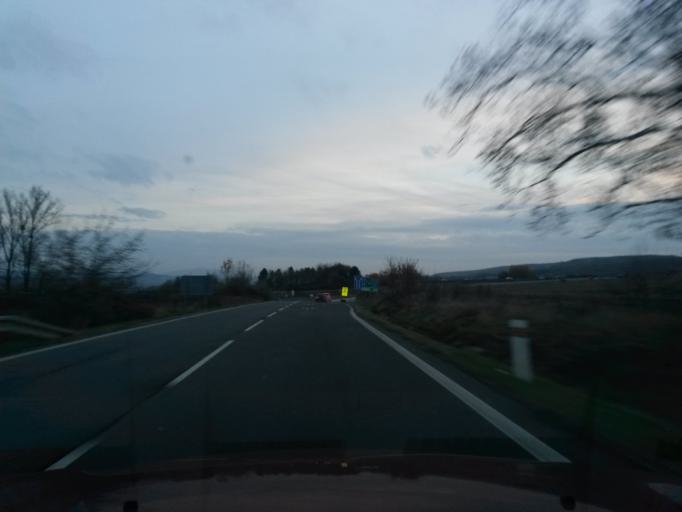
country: SK
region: Kosicky
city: Kosice
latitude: 48.7911
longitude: 21.3070
